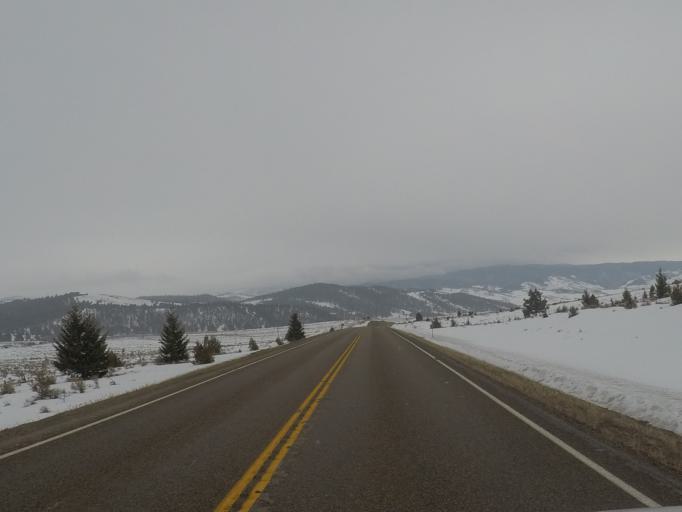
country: US
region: Montana
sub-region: Meagher County
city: White Sulphur Springs
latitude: 46.6345
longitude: -110.8544
